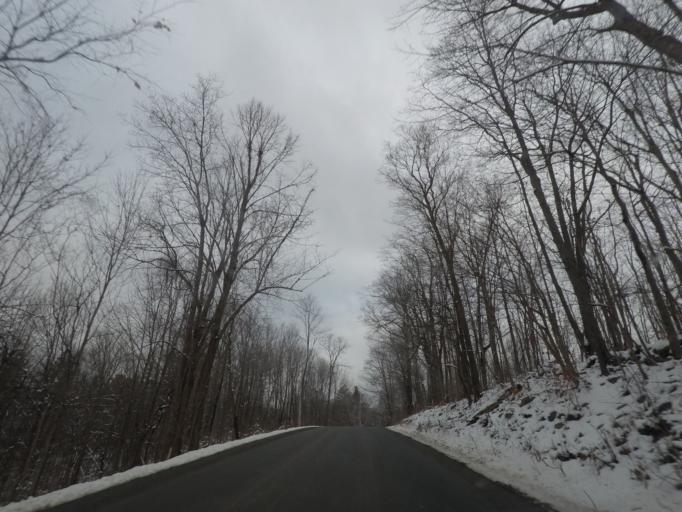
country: US
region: New York
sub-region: Rensselaer County
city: Averill Park
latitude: 42.6538
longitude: -73.5329
